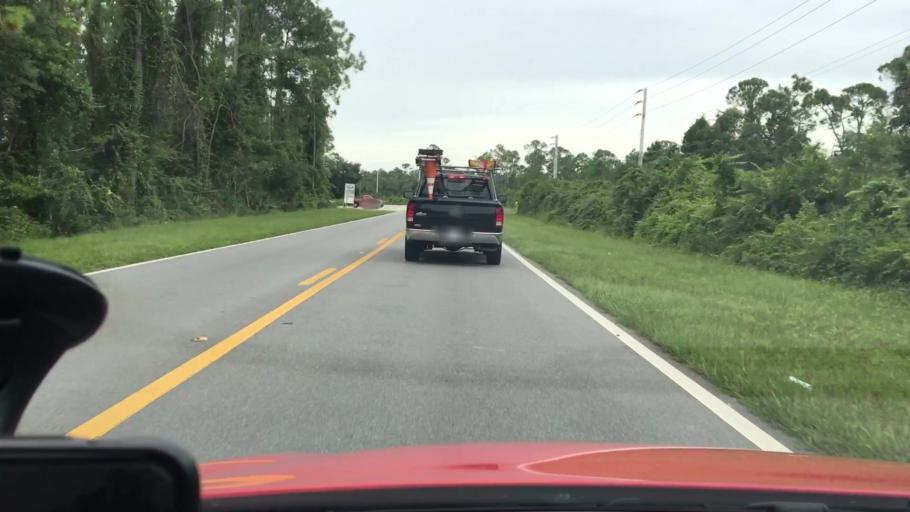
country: US
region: Florida
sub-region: Flagler County
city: Flagler Beach
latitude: 29.5018
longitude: -81.1908
